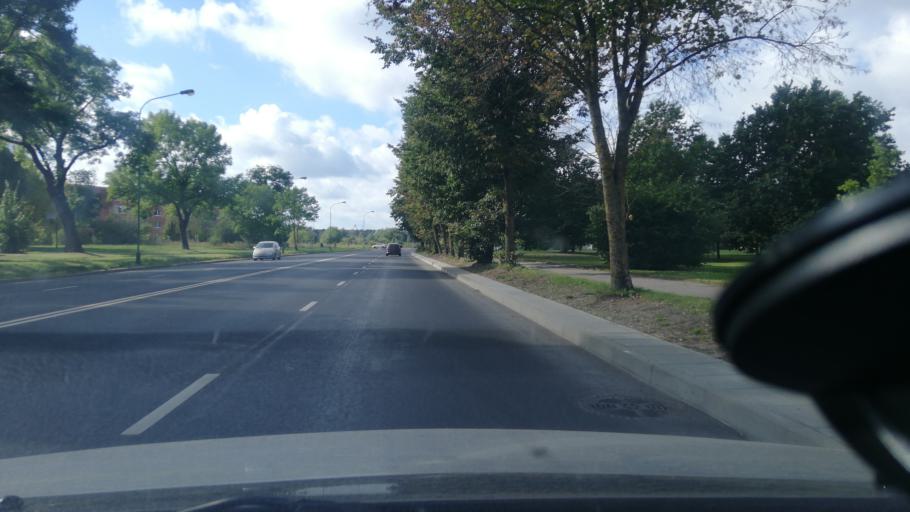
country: LT
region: Klaipedos apskritis
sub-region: Klaipeda
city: Klaipeda
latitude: 55.6658
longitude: 21.1720
